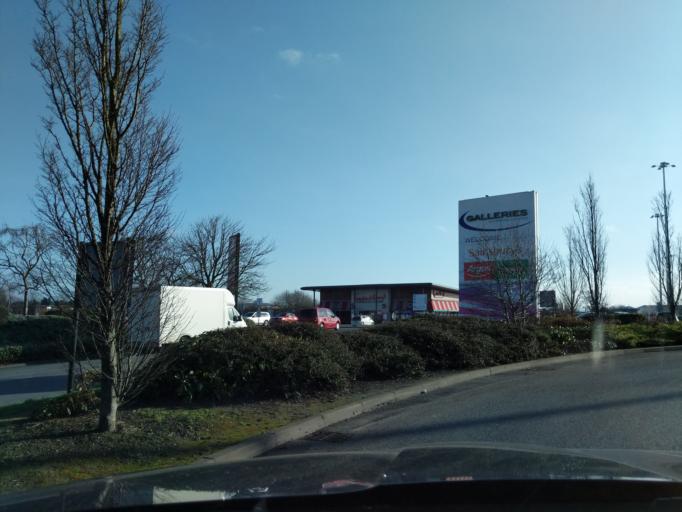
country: GB
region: England
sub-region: Sunderland
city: Washington
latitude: 54.9022
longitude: -1.5311
